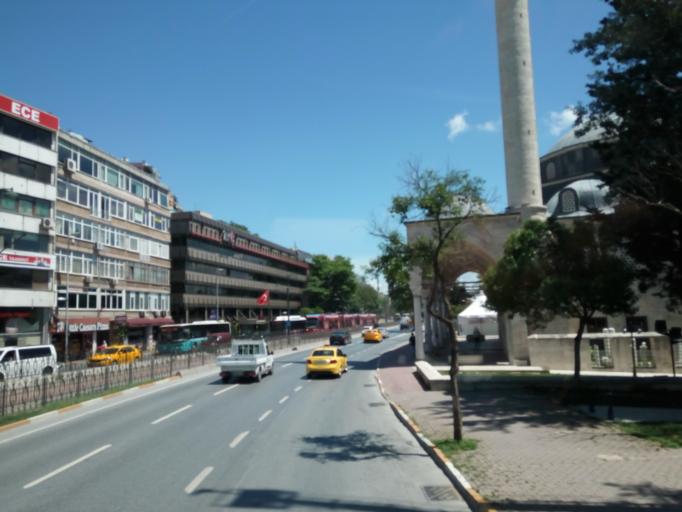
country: TR
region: Istanbul
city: Eminoenue
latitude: 41.0319
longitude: 28.9900
